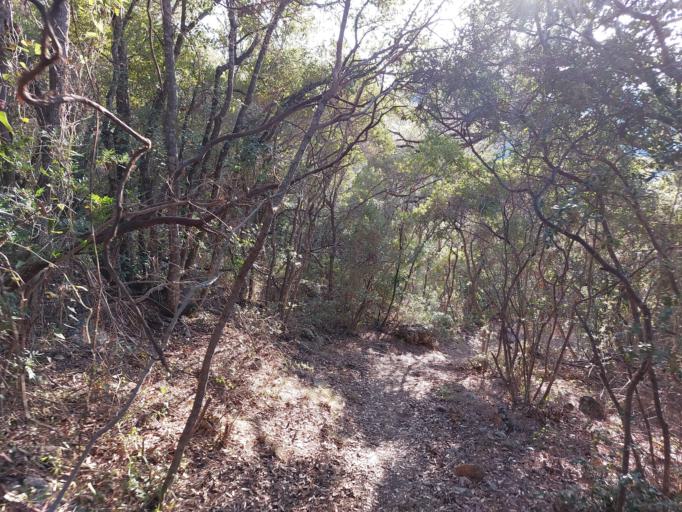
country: HR
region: Dubrovacko-Neretvanska
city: Smokvica
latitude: 42.7650
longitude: 16.8022
